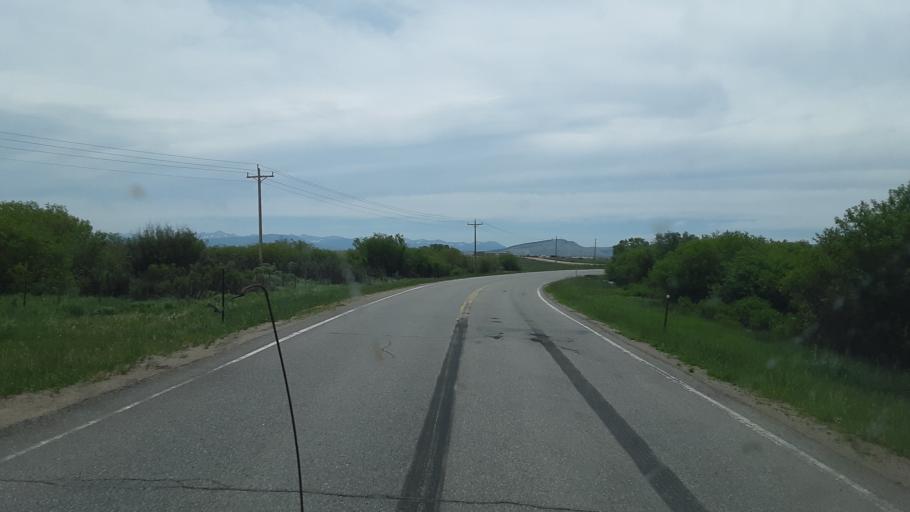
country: US
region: Colorado
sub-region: Jackson County
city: Walden
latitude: 40.5445
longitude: -106.3993
